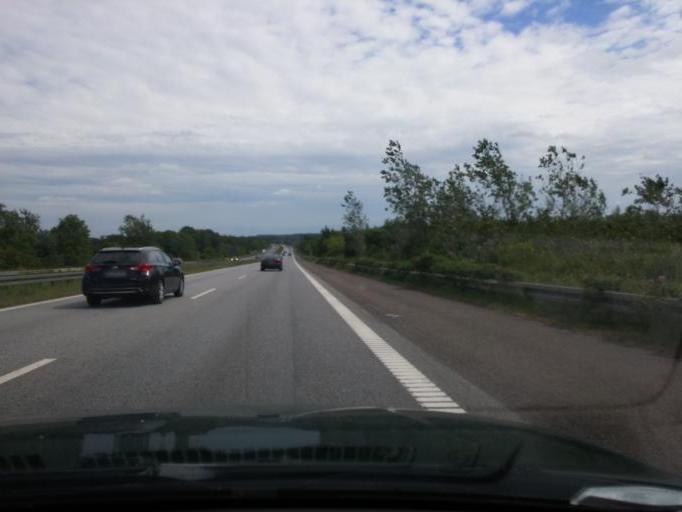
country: DK
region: South Denmark
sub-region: Middelfart Kommune
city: Ejby
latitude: 55.4451
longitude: 9.9643
